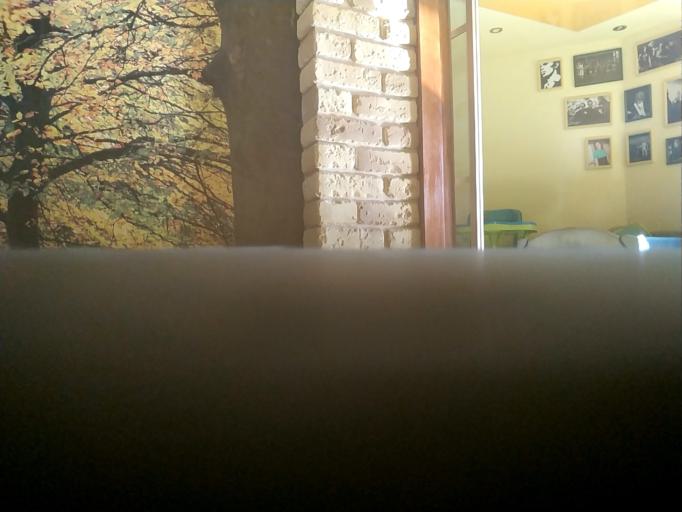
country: RU
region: Smolensk
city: Temkino
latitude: 54.9406
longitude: 34.9602
